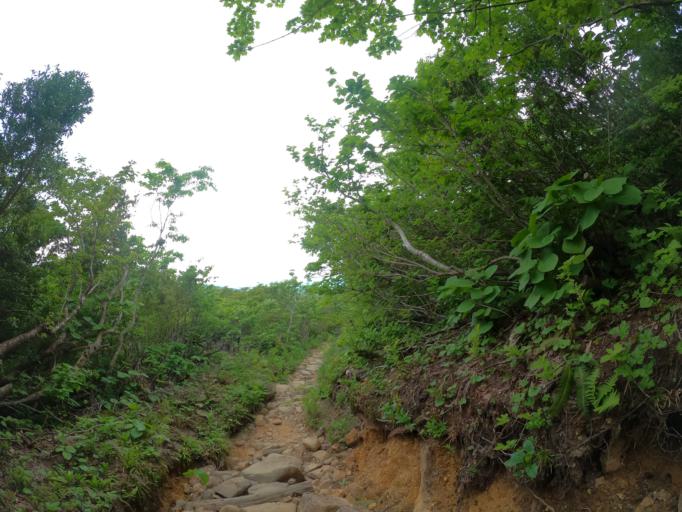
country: JP
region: Akita
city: Yuzawa
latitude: 38.9718
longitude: 140.7862
